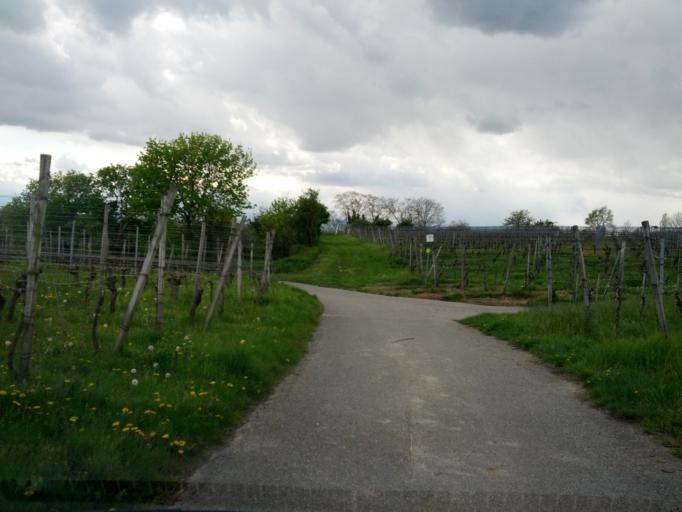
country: DE
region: Baden-Wuerttemberg
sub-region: Freiburg Region
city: Merdingen
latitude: 47.9937
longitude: 7.6778
